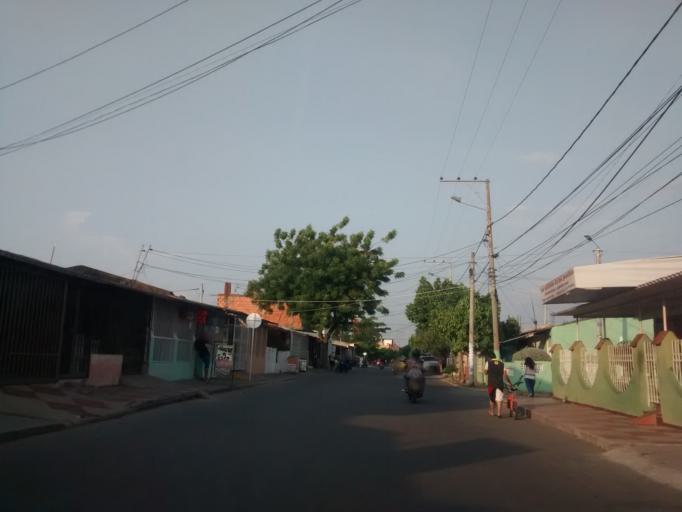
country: CO
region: Cundinamarca
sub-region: Girardot
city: Girardot City
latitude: 4.3145
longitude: -74.7871
